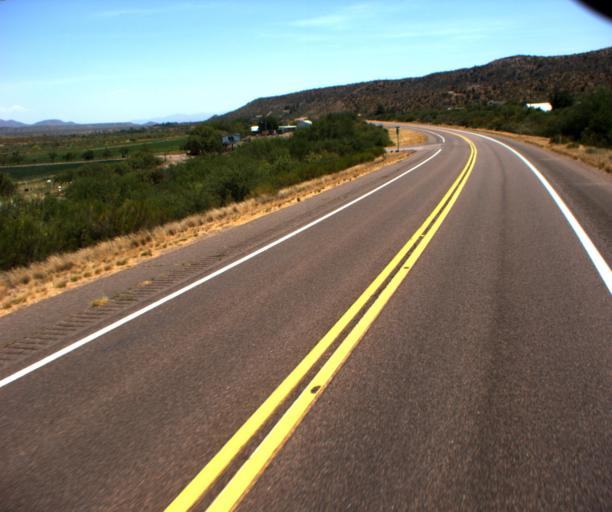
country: US
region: Arizona
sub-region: Gila County
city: Tonto Basin
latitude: 33.9615
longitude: -111.3258
